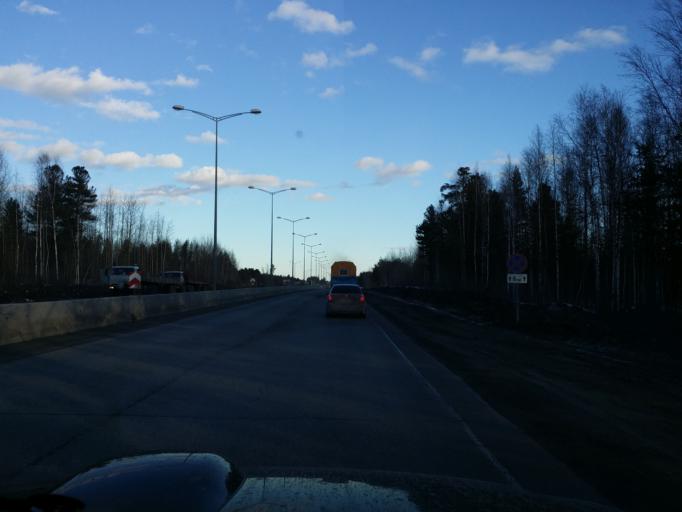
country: RU
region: Khanty-Mansiyskiy Avtonomnyy Okrug
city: Nizhnevartovsk
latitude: 61.0105
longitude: 76.4016
